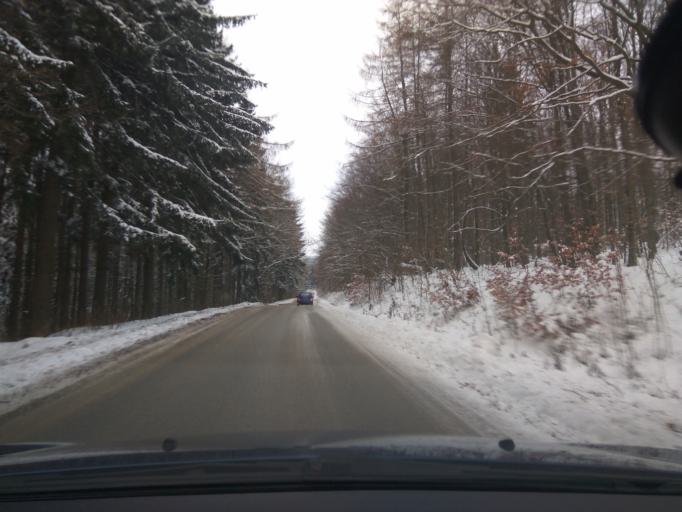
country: CZ
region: Zlin
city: Strani
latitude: 48.8474
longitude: 17.6904
